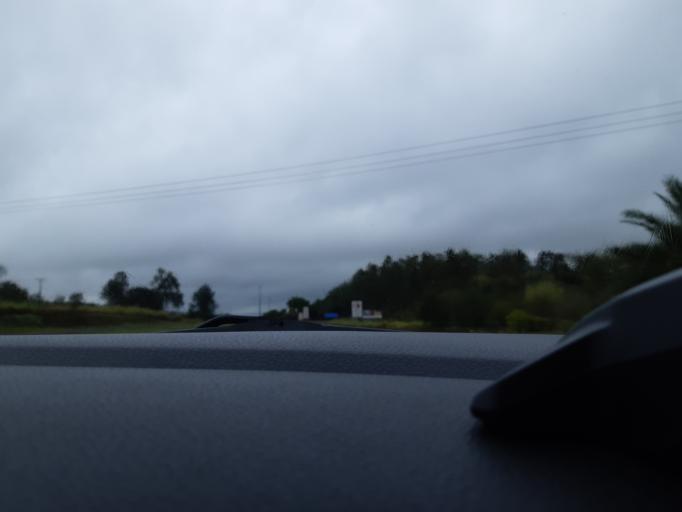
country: BR
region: Sao Paulo
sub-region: Ourinhos
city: Ourinhos
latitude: -22.9937
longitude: -49.9046
